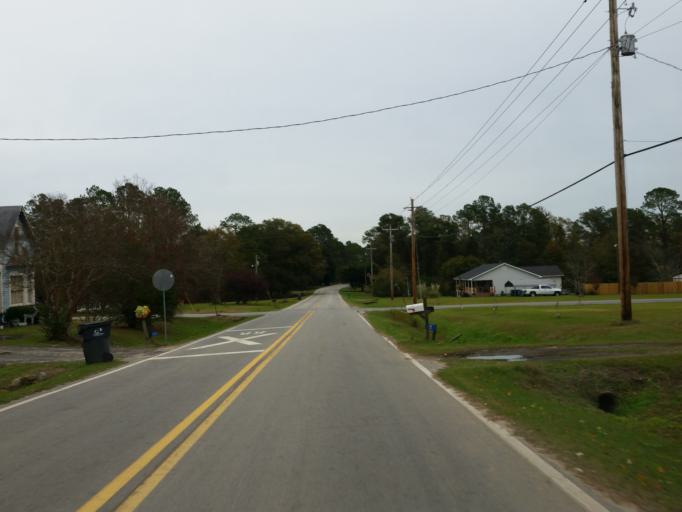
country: US
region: Georgia
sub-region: Crisp County
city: Cordele
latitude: 31.8340
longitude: -83.7392
